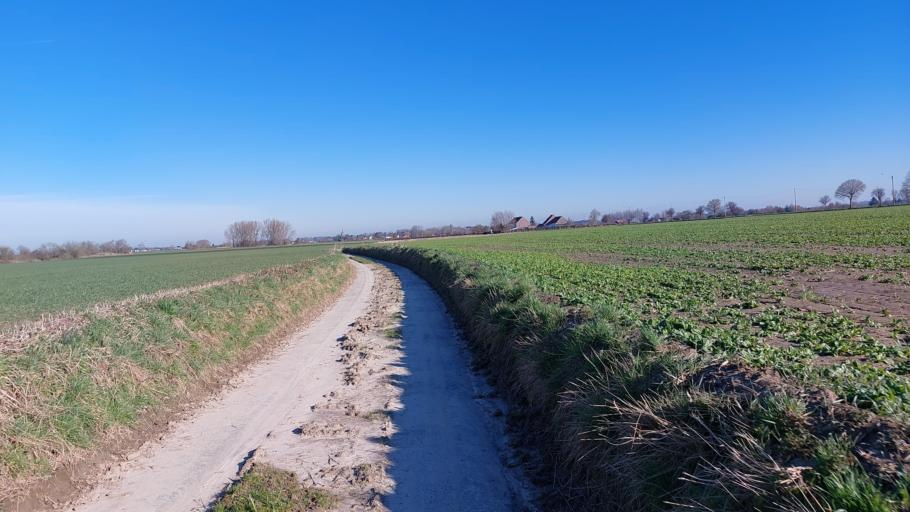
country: BE
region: Wallonia
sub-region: Province du Hainaut
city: Chievres
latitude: 50.5652
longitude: 3.8037
